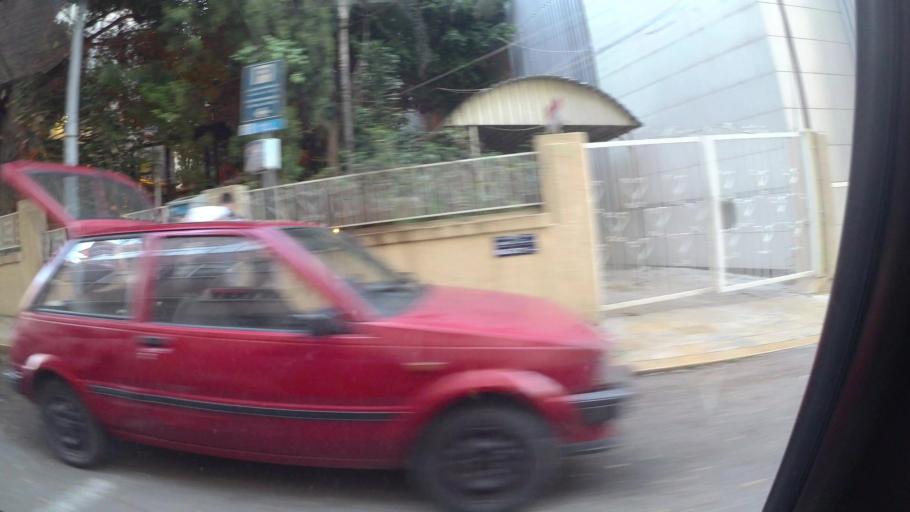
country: LB
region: Beyrouth
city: Ra's Bayrut
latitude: 33.8976
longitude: 35.4911
